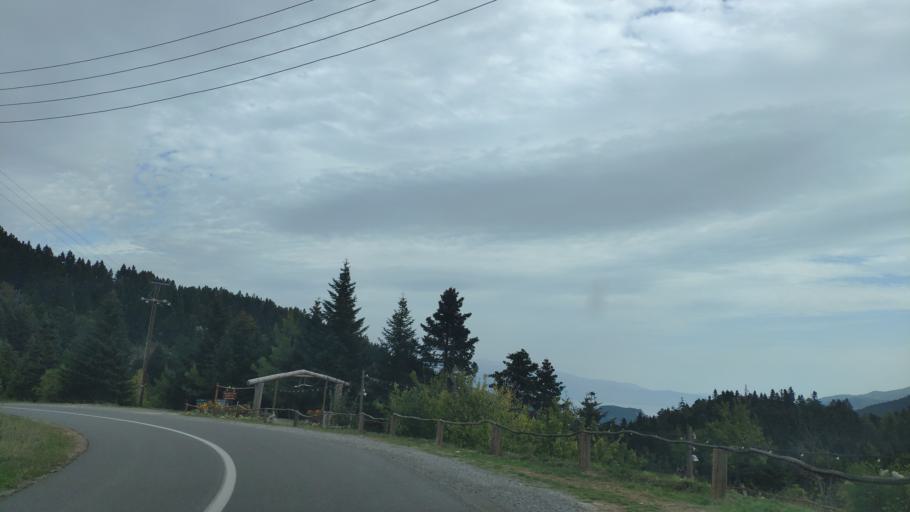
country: GR
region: Central Greece
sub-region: Nomos Fthiotidos
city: Stavros
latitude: 38.7287
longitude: 22.3389
